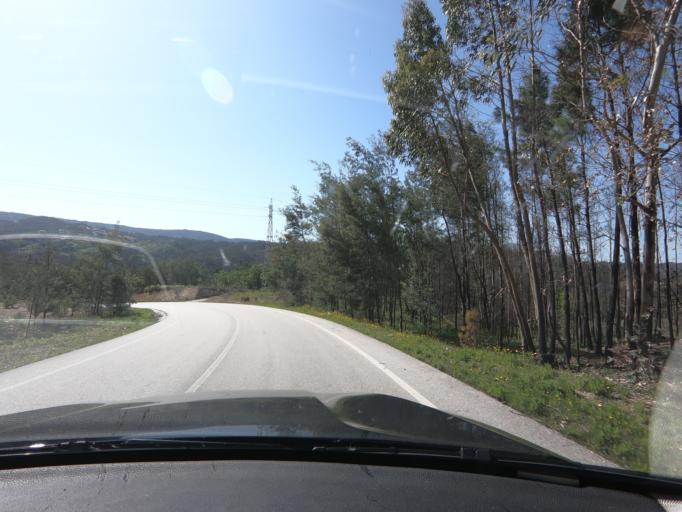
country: PT
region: Coimbra
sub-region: Penacova
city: Penacova
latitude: 40.2932
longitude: -8.2509
